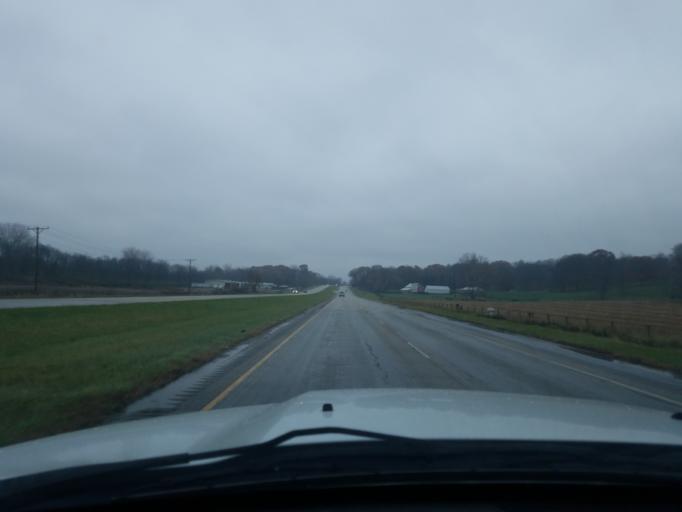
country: US
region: Indiana
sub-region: Cass County
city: Logansport
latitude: 40.7324
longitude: -86.3249
